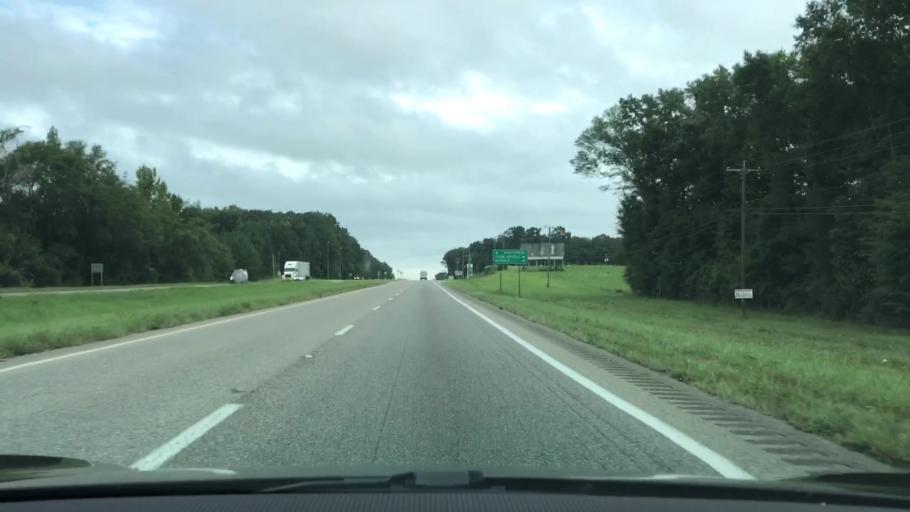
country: US
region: Alabama
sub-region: Montgomery County
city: Pike Road
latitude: 32.1894
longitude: -86.1173
